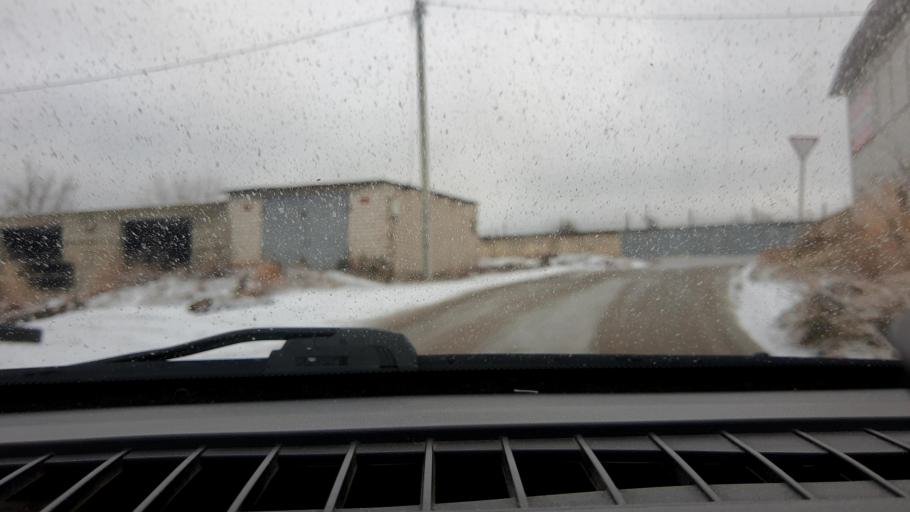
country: RU
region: Nizjnij Novgorod
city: Taremskoye
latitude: 55.9410
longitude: 43.0626
